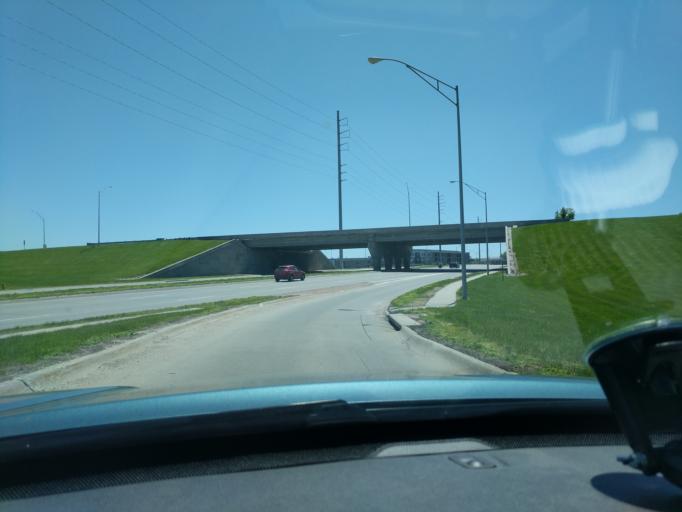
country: US
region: Nebraska
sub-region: Douglas County
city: Ralston
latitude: 41.2354
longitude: -96.0243
